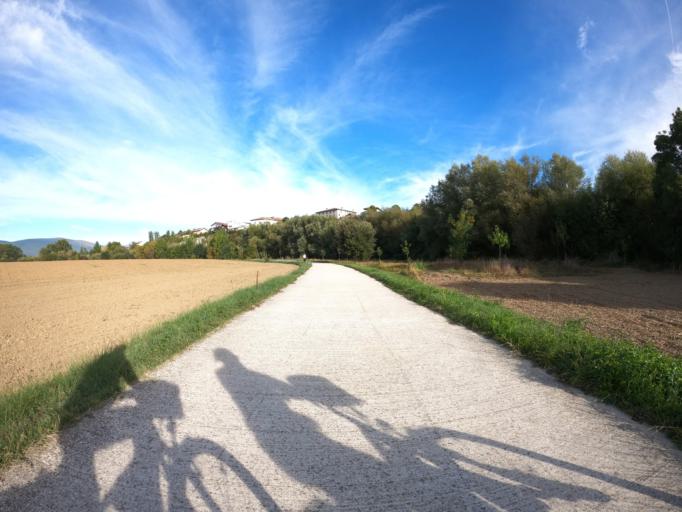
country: ES
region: Navarre
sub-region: Provincia de Navarra
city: Orkoien
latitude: 42.8140
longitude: -1.7213
